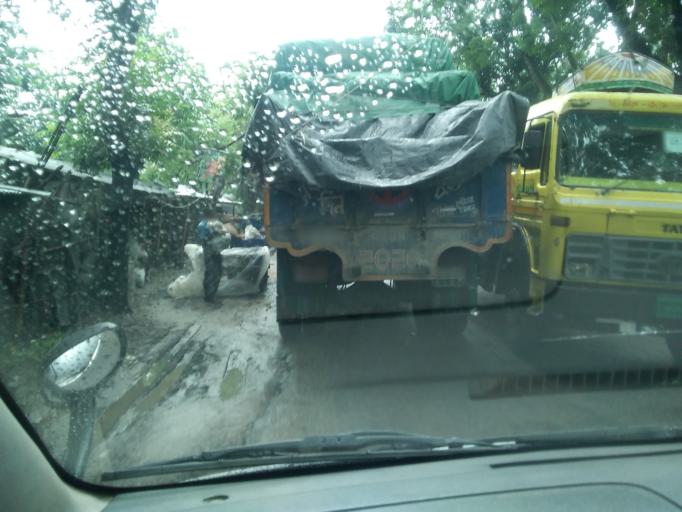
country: IN
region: West Bengal
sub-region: North 24 Parganas
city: Taki
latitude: 22.3471
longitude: 89.1039
